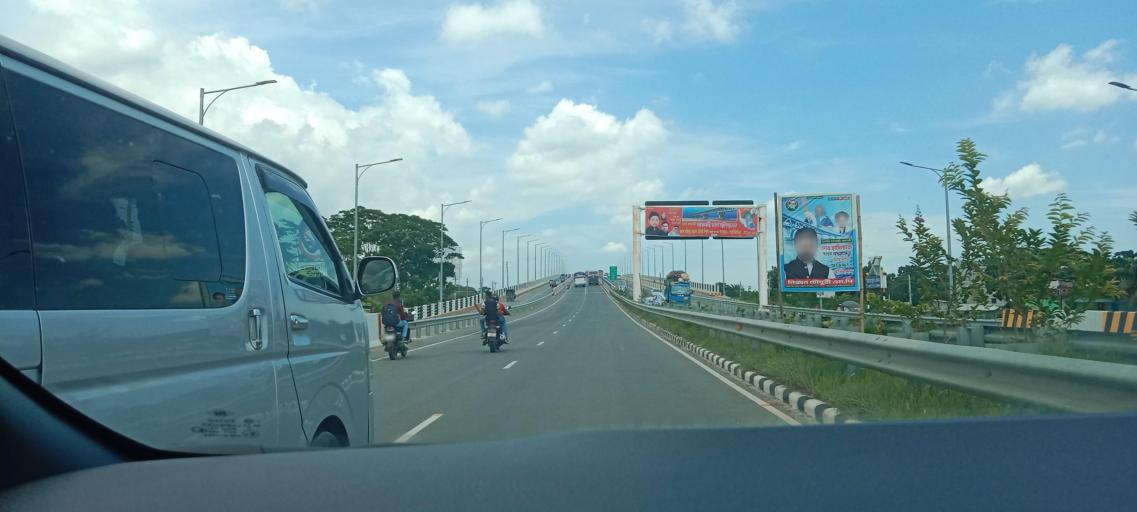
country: BD
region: Dhaka
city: Char Bhadrasan
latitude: 23.3868
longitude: 89.9914
